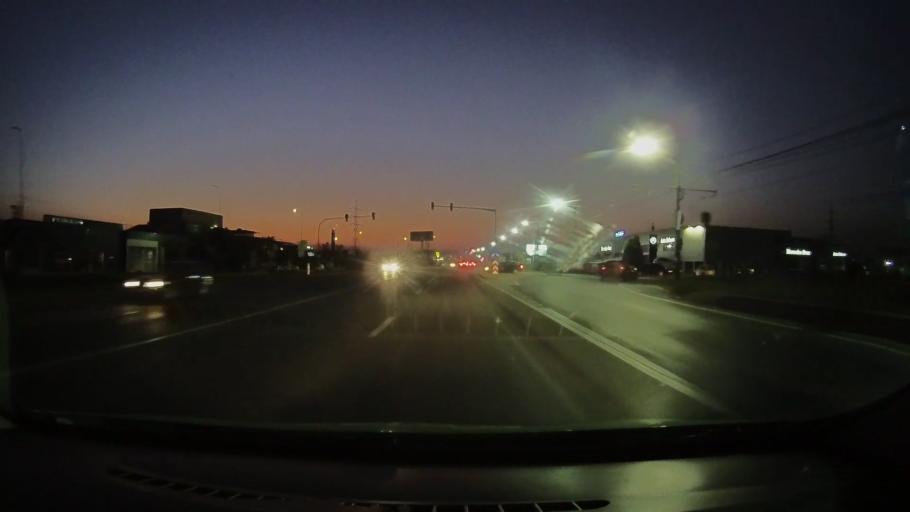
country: RO
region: Arad
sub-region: Comuna Vladimirescu
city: Vladimirescu
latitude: 46.1744
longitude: 21.3710
